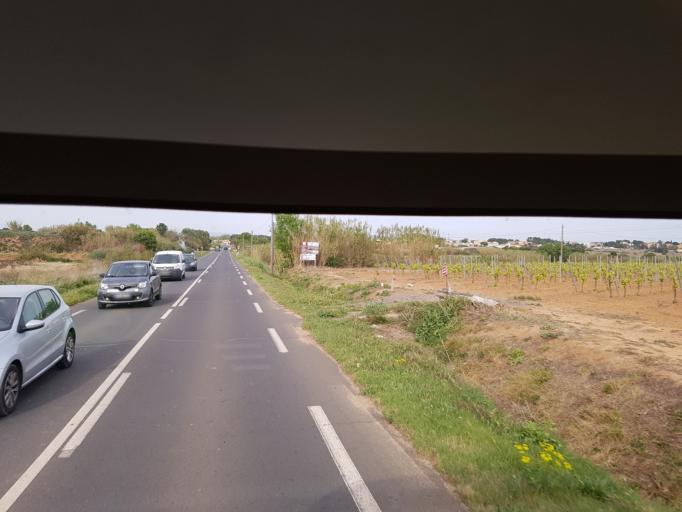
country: FR
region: Languedoc-Roussillon
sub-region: Departement de l'Herault
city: Marseillan
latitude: 43.3505
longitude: 3.5123
